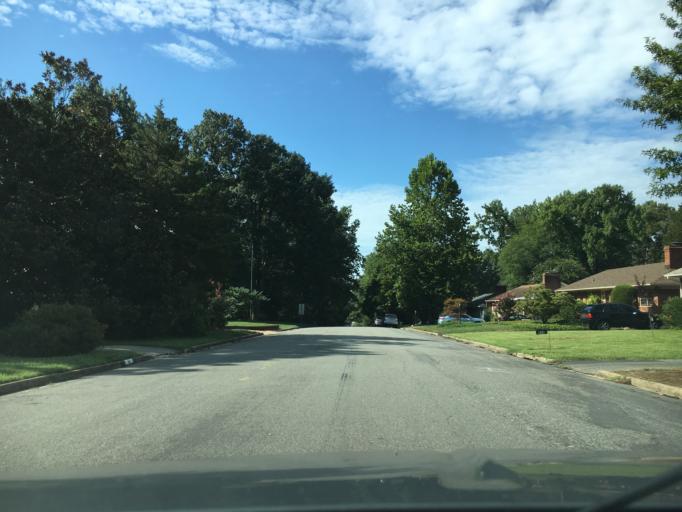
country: US
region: Virginia
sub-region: Henrico County
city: Tuckahoe
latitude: 37.5888
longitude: -77.5361
